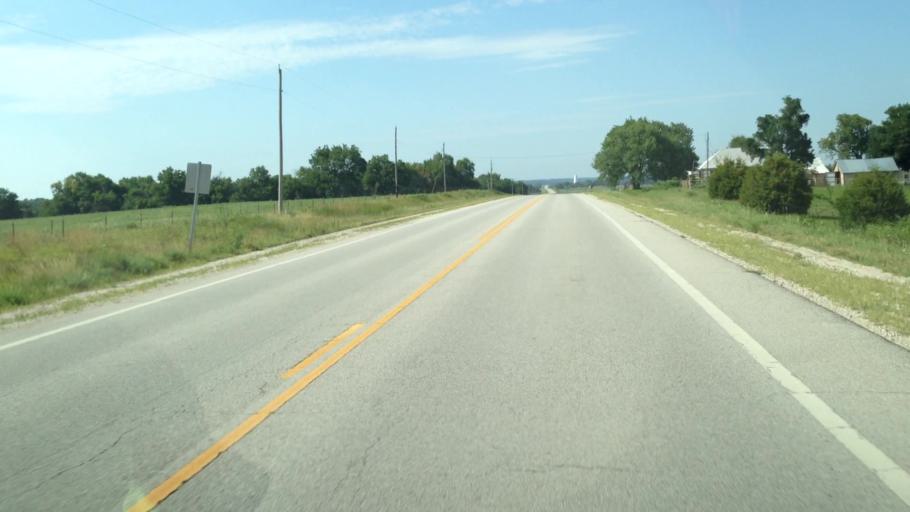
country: US
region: Kansas
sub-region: Neosho County
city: Erie
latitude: 37.4758
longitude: -95.2692
